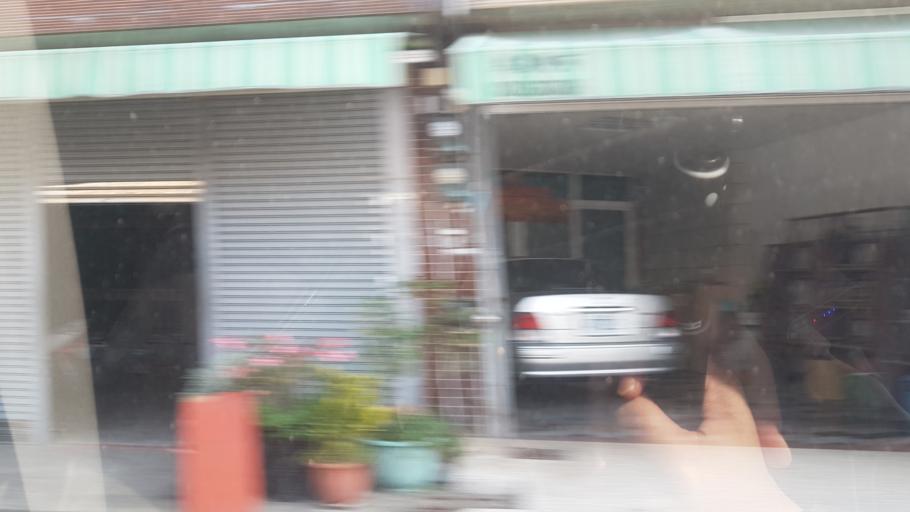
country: TW
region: Taiwan
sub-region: Tainan
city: Tainan
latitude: 22.9396
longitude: 120.2487
